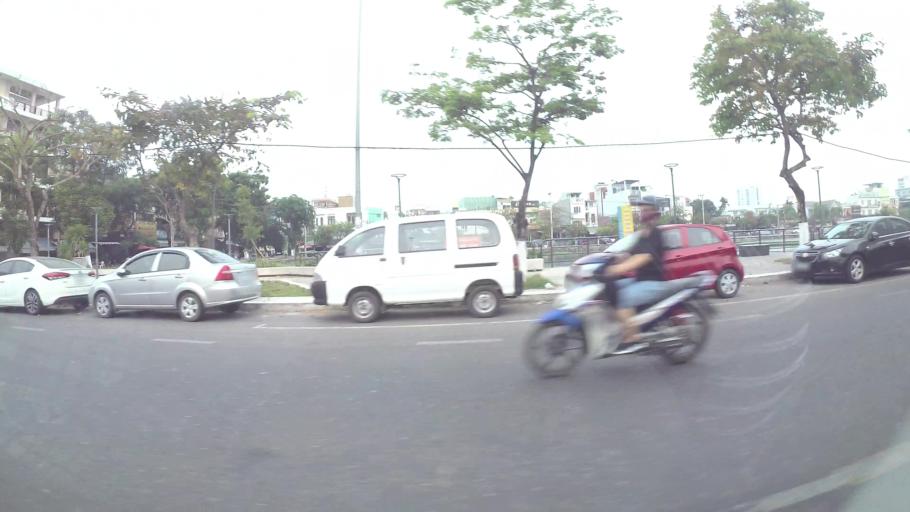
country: VN
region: Da Nang
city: Da Nang
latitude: 16.0640
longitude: 108.2106
